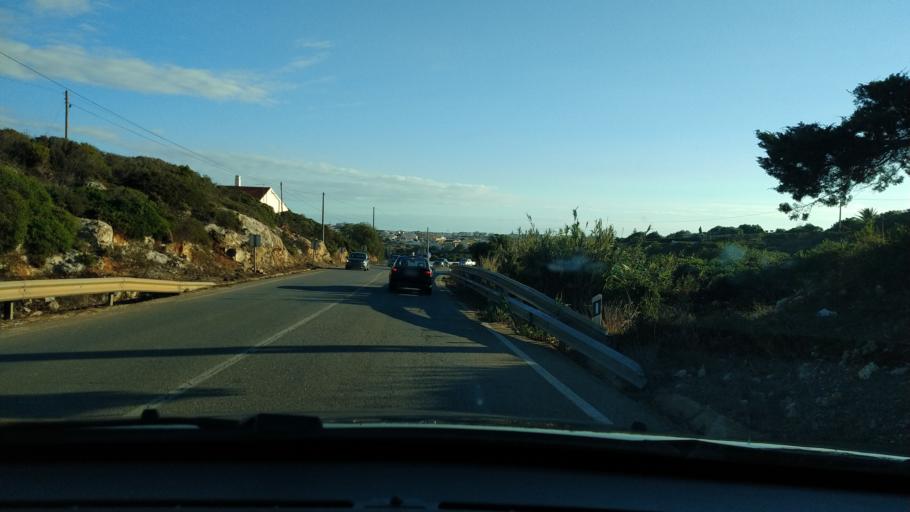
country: PT
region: Faro
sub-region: Vila do Bispo
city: Sagres
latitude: 37.0236
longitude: -8.9378
